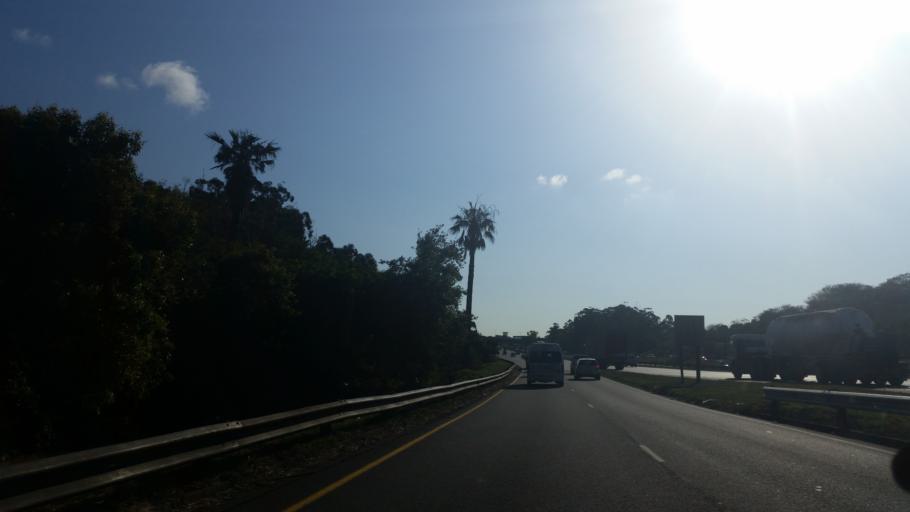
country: ZA
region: KwaZulu-Natal
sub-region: eThekwini Metropolitan Municipality
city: Berea
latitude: -29.8372
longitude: 30.9582
